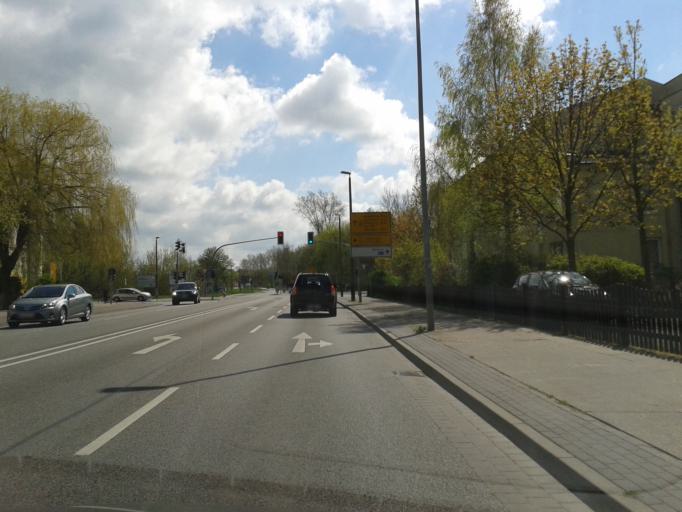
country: DE
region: Saxony-Anhalt
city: Salzwedel
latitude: 52.8517
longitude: 11.1621
